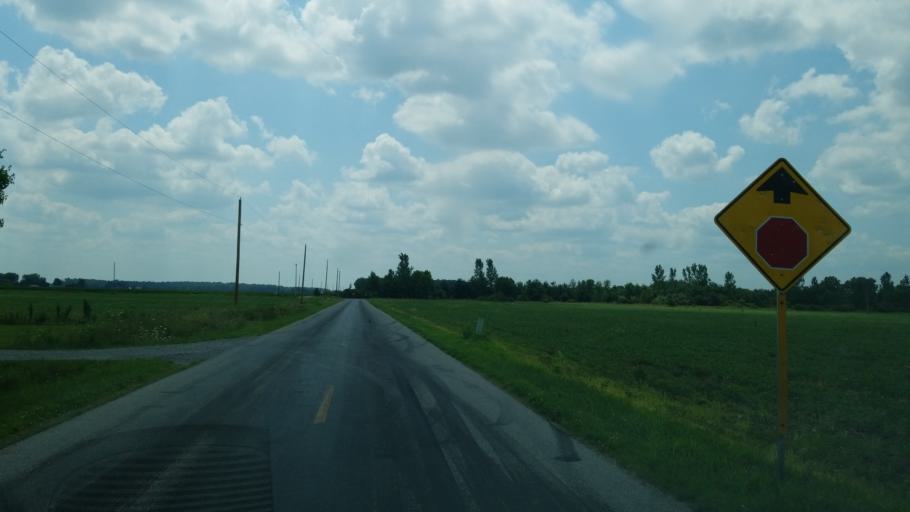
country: US
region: Ohio
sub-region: Henry County
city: Napoleon
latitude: 41.3436
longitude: -84.1346
